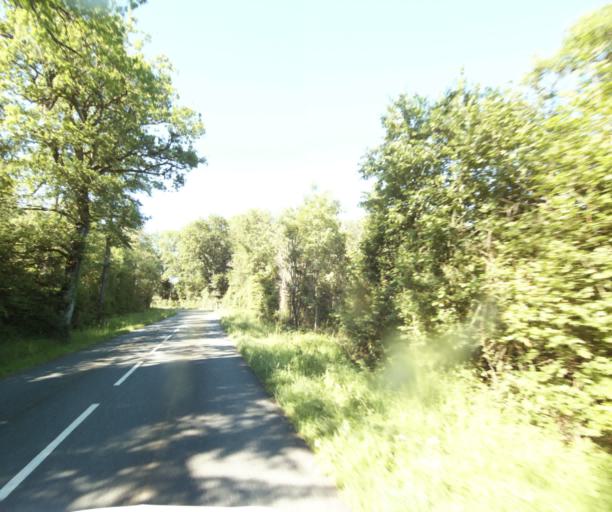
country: FR
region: Rhone-Alpes
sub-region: Departement de la Haute-Savoie
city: Ballaison
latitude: 46.2889
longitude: 6.3435
